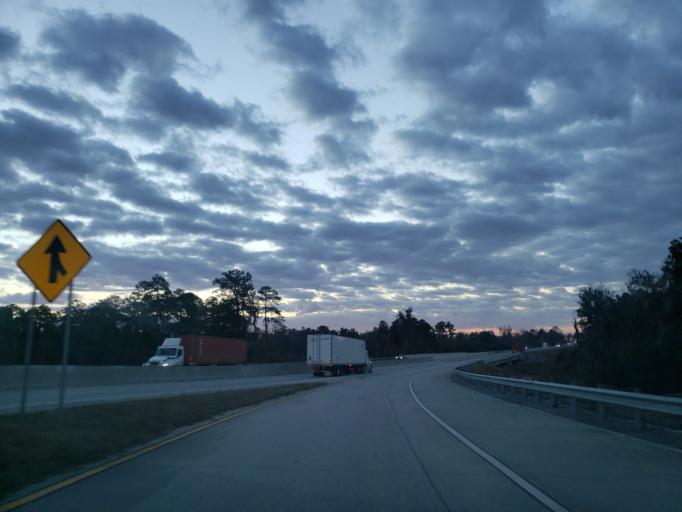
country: US
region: Georgia
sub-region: Chatham County
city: Port Wentworth
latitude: 32.1619
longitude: -81.1784
